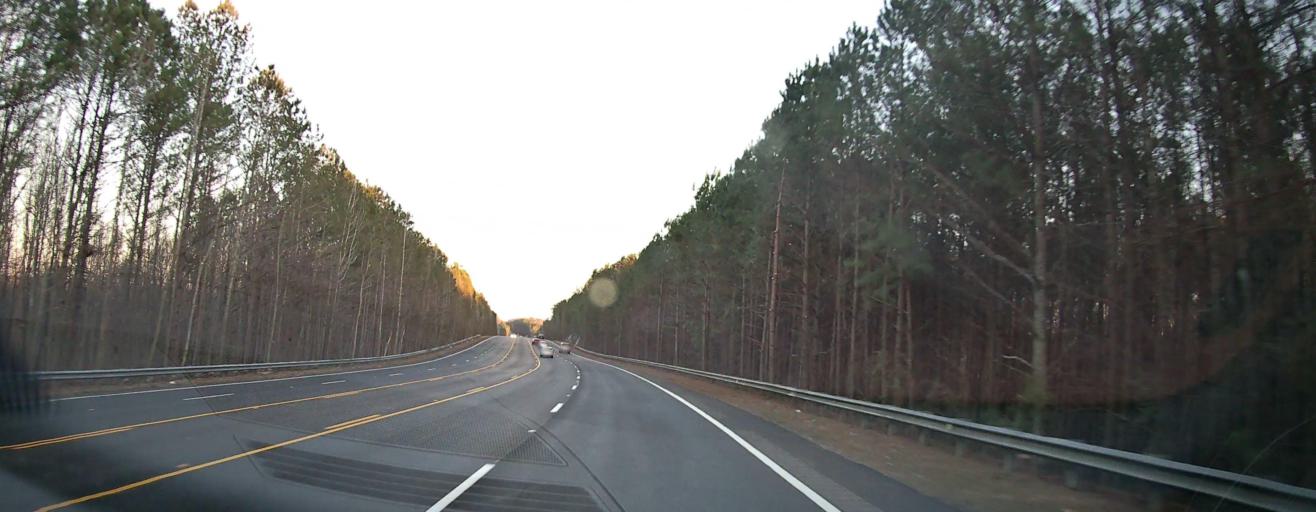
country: US
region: Georgia
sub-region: Fulton County
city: Union City
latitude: 33.5521
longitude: -84.4962
